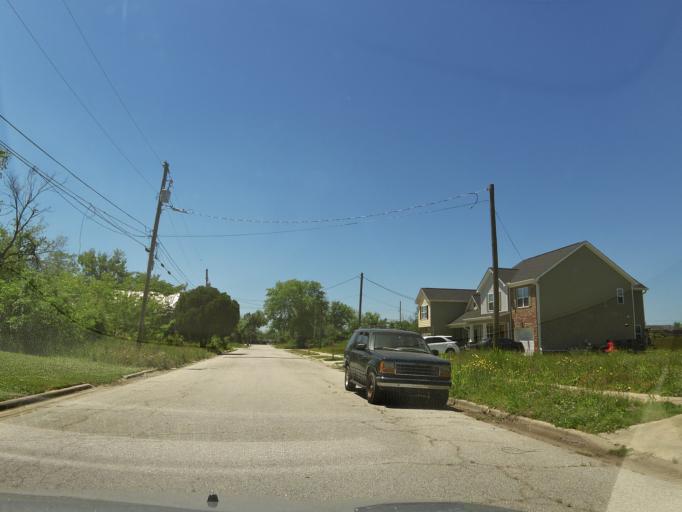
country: US
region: Georgia
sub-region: Richmond County
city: Augusta
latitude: 33.4655
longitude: -81.9717
